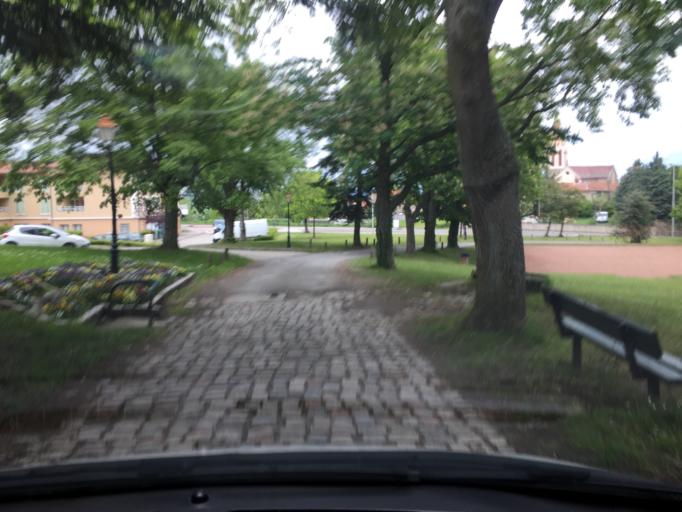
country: FR
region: Rhone-Alpes
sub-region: Departement du Rhone
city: Saint-Maurice-sur-Dargoire
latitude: 45.5821
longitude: 4.6290
